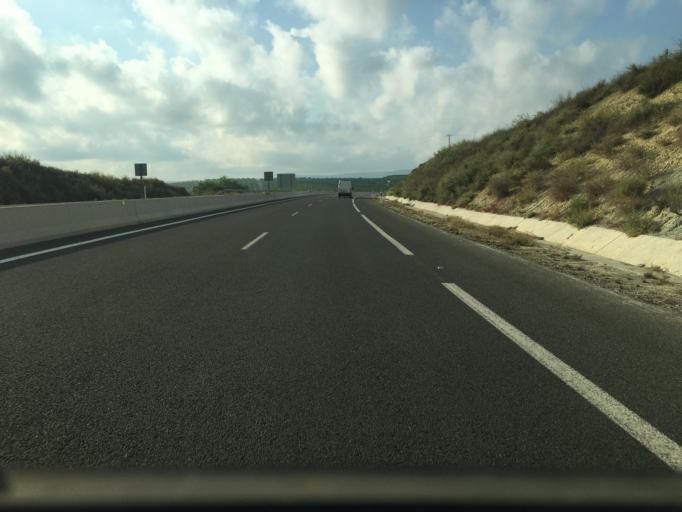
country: ES
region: Murcia
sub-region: Murcia
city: Beniel
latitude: 37.9941
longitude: -0.9777
